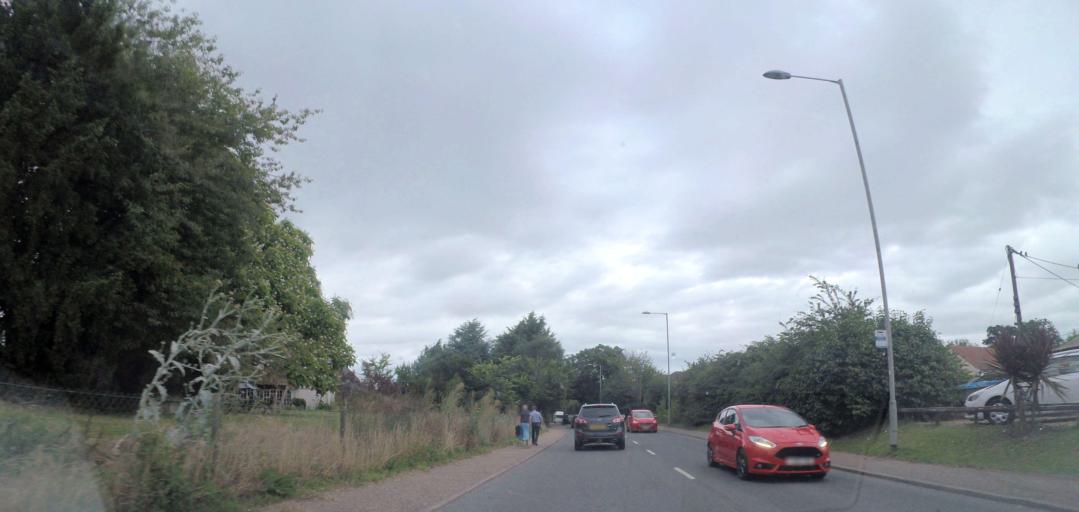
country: GB
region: England
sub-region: Norfolk
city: Coltishall
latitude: 52.7236
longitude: 1.3504
